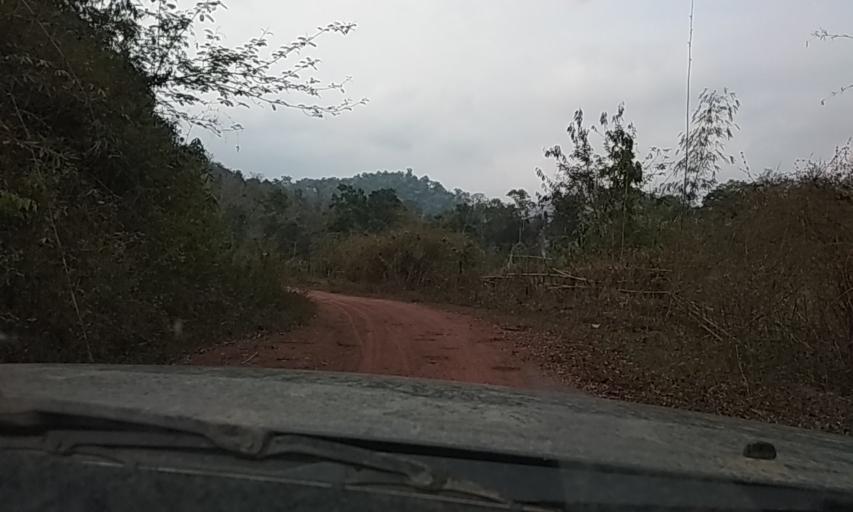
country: TH
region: Nan
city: Mae Charim
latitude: 18.4538
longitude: 101.1956
